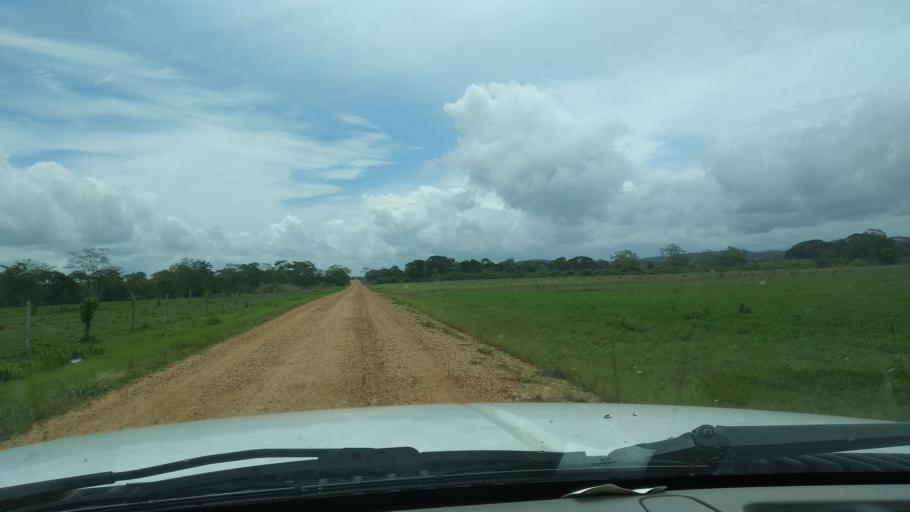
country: BZ
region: Cayo
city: San Ignacio
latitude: 17.2263
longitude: -88.9789
